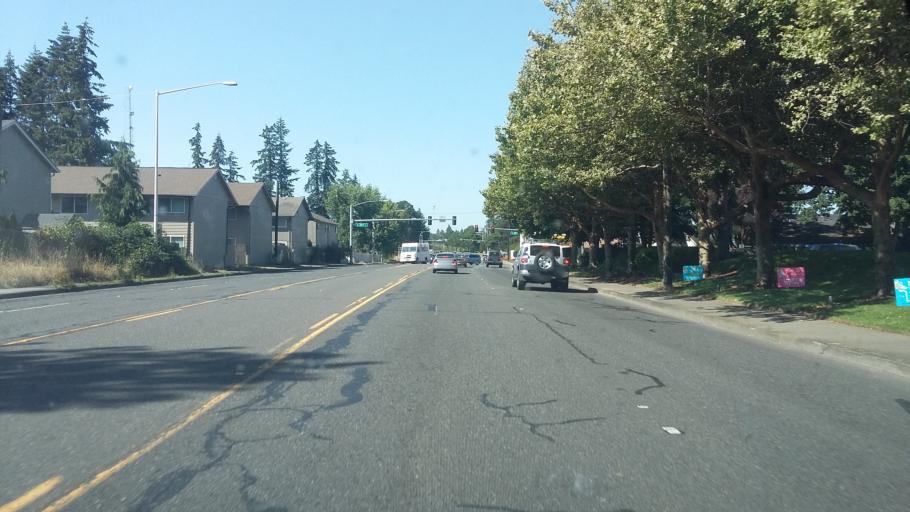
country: US
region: Washington
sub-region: Clark County
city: Orchards
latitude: 45.6559
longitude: -122.5579
